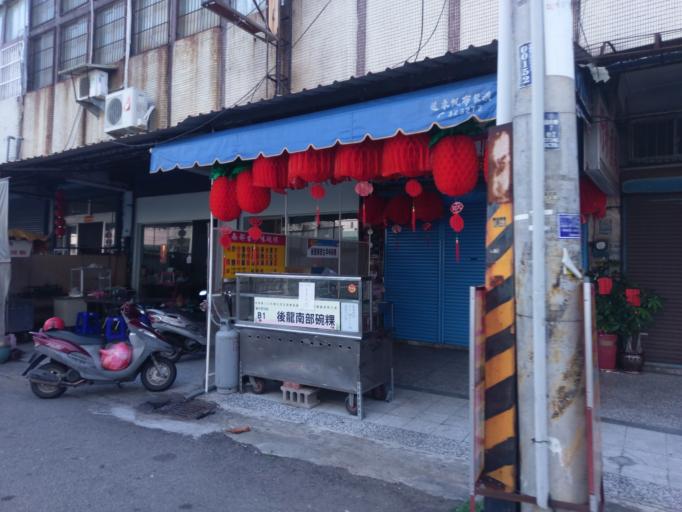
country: TW
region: Taiwan
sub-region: Miaoli
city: Miaoli
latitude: 24.6142
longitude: 120.7884
